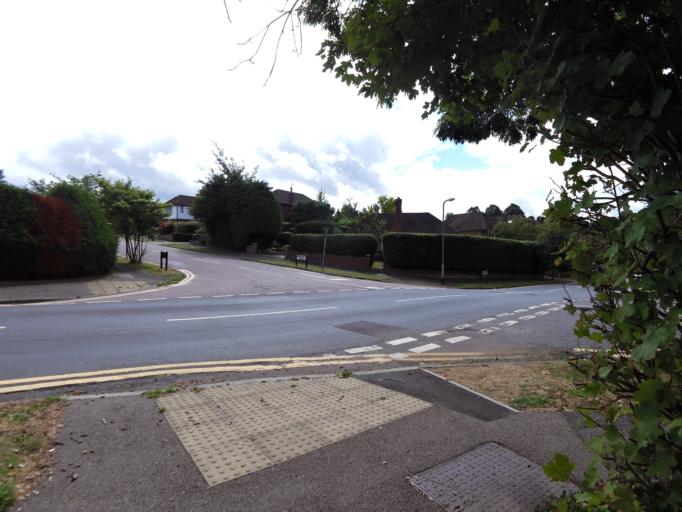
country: GB
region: England
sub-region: Hertfordshire
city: Radlett
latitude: 51.6831
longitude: -0.3113
